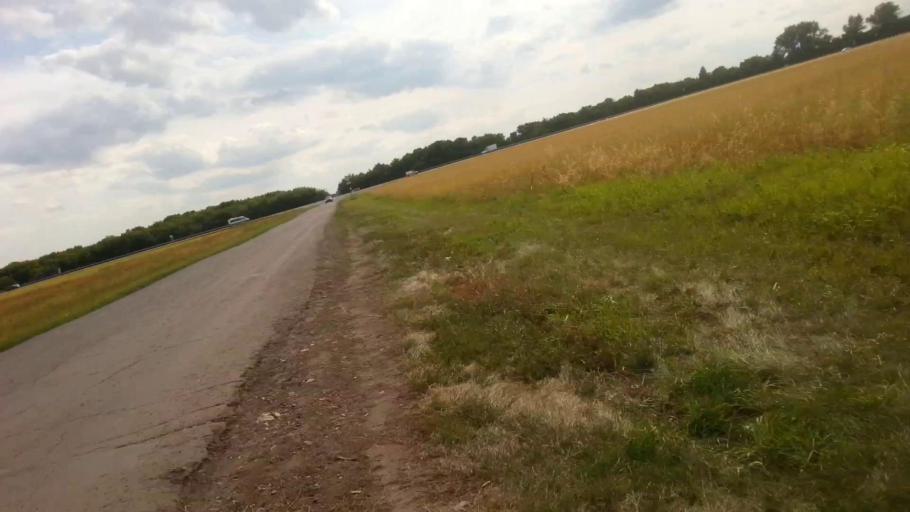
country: RU
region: Altai Krai
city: Nauchnyy Gorodok
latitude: 53.3591
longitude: 83.5087
